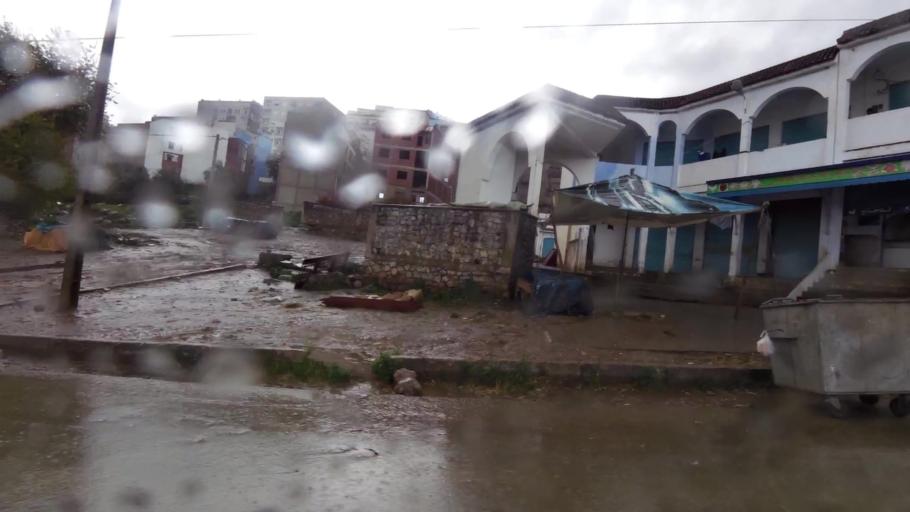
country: MA
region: Tanger-Tetouan
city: Chefchaouene
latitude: 35.1649
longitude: -5.2686
